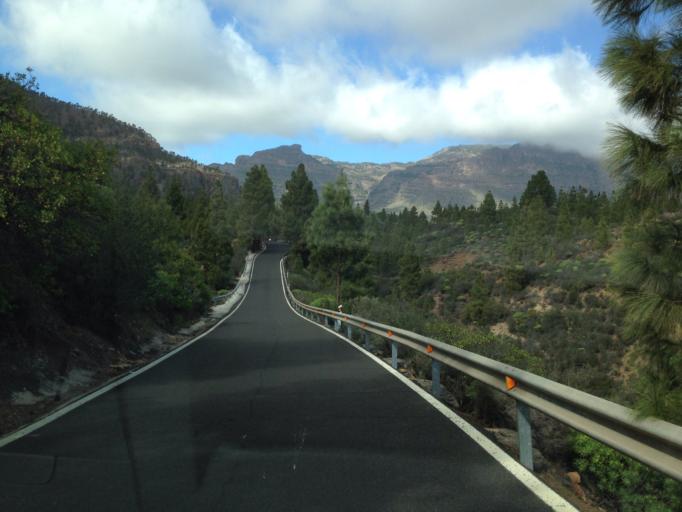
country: ES
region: Canary Islands
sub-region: Provincia de Las Palmas
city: San Bartolome
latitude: 27.9127
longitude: -15.5727
